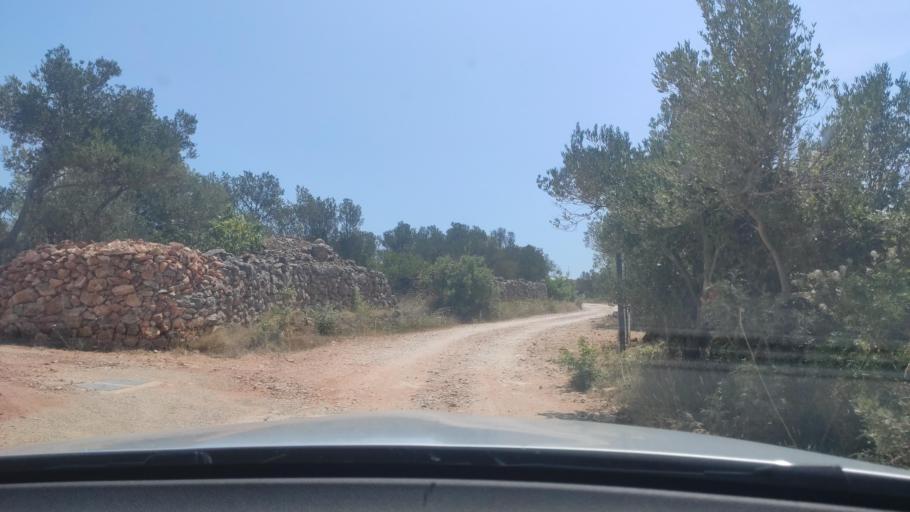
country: HR
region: Sibensko-Kniniska
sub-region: Grad Sibenik
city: Tisno
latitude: 43.7795
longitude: 15.6442
